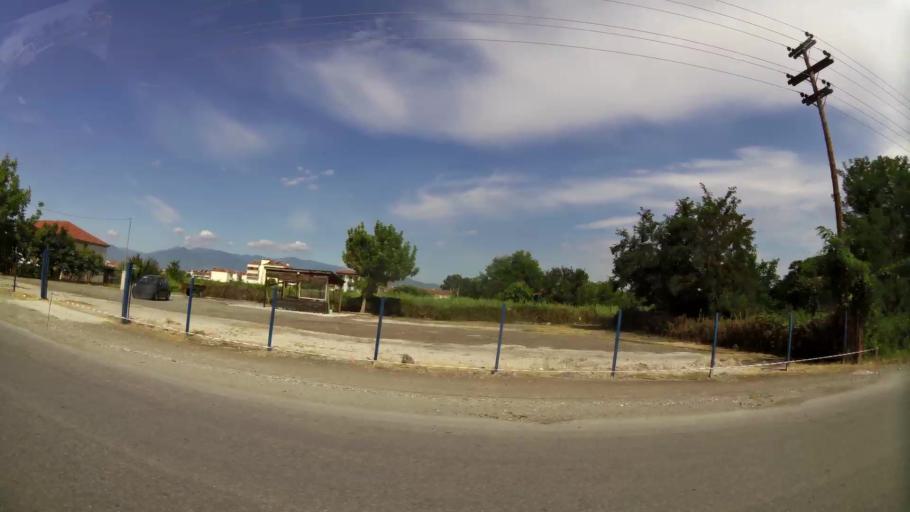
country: GR
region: Central Macedonia
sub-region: Nomos Pierias
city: Katerini
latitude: 40.2833
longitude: 22.5188
